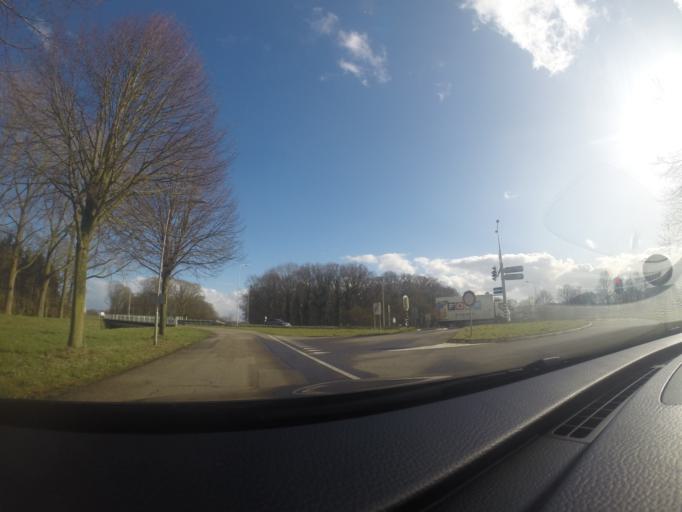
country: NL
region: Gelderland
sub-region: Oude IJsselstreek
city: Varsseveld
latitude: 51.9534
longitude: 6.4692
